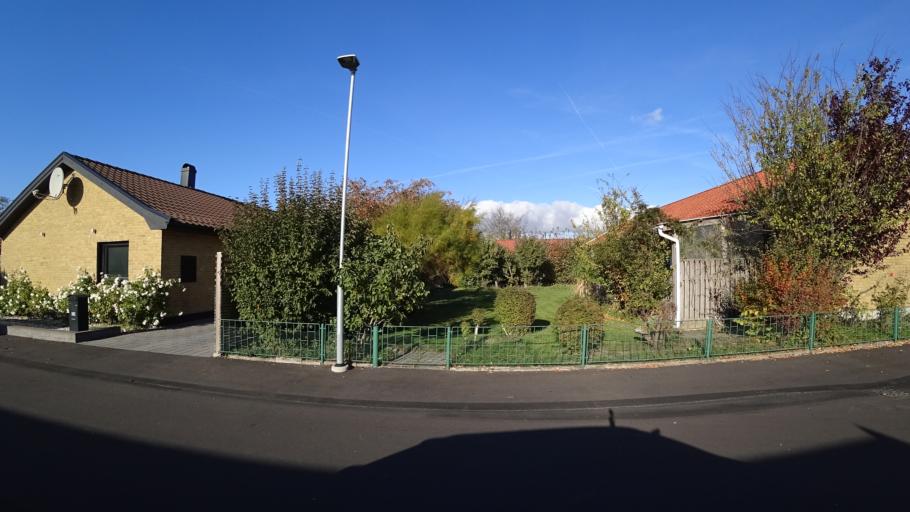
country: SE
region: Skane
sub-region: Staffanstorps Kommun
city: Hjaerup
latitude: 55.6655
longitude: 13.1464
